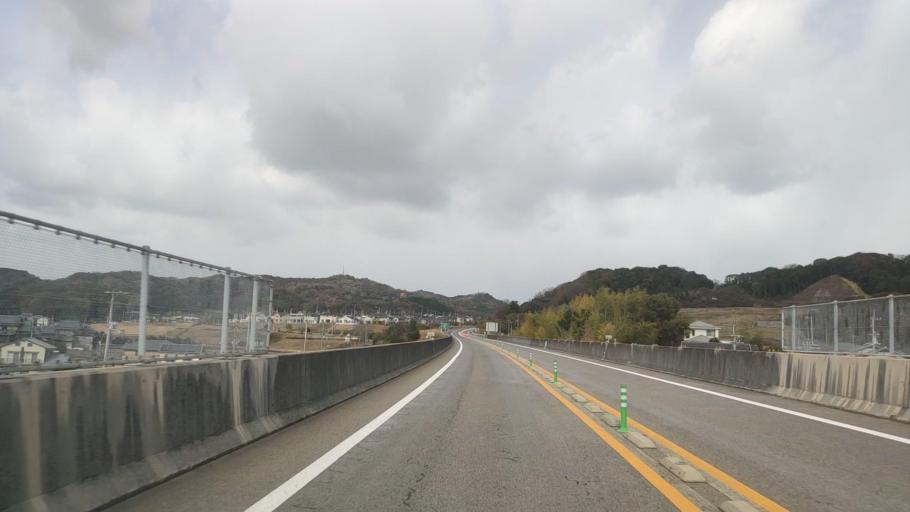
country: JP
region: Ehime
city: Hojo
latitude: 34.0630
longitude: 132.9730
